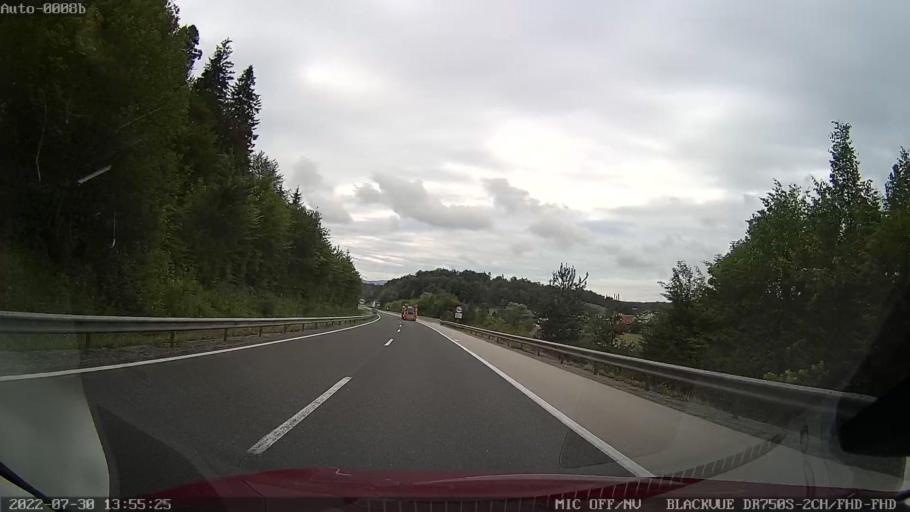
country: SI
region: Grosuplje
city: Grosuplje
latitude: 45.9762
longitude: 14.6784
